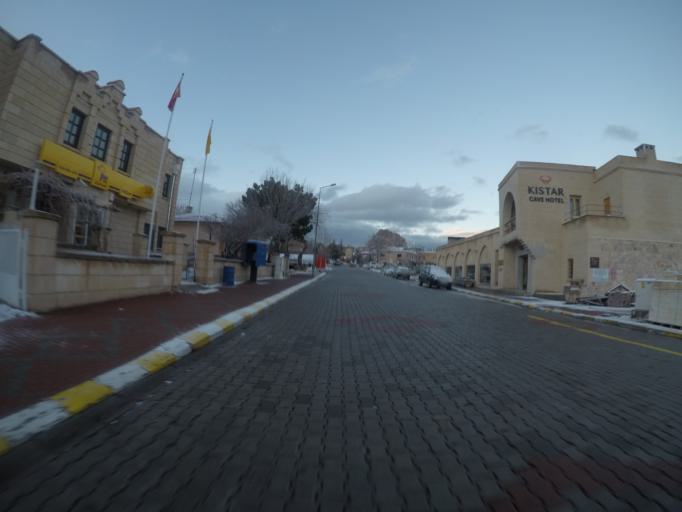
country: TR
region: Nevsehir
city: Goereme
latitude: 38.6263
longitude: 34.8044
